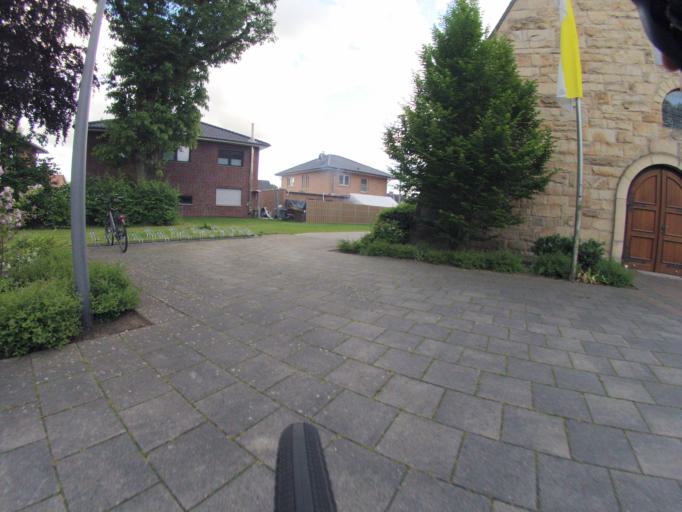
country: DE
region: North Rhine-Westphalia
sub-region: Regierungsbezirk Munster
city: Birgte
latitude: 52.2972
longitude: 7.6584
